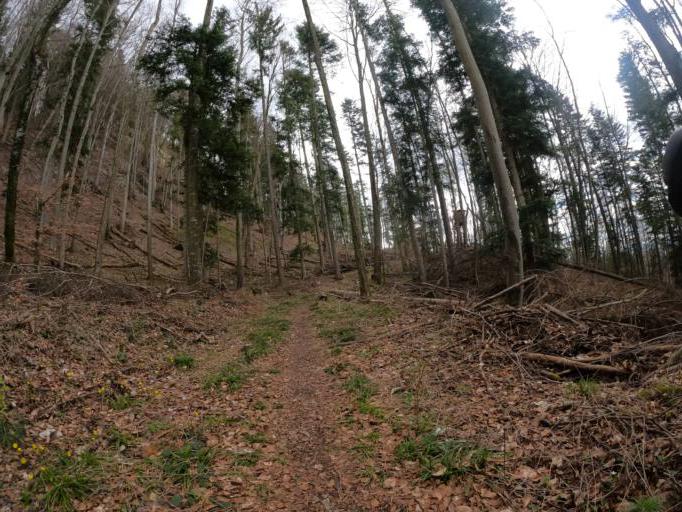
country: DE
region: Baden-Wuerttemberg
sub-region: Tuebingen Region
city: Jungingen
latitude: 48.3632
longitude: 9.0562
